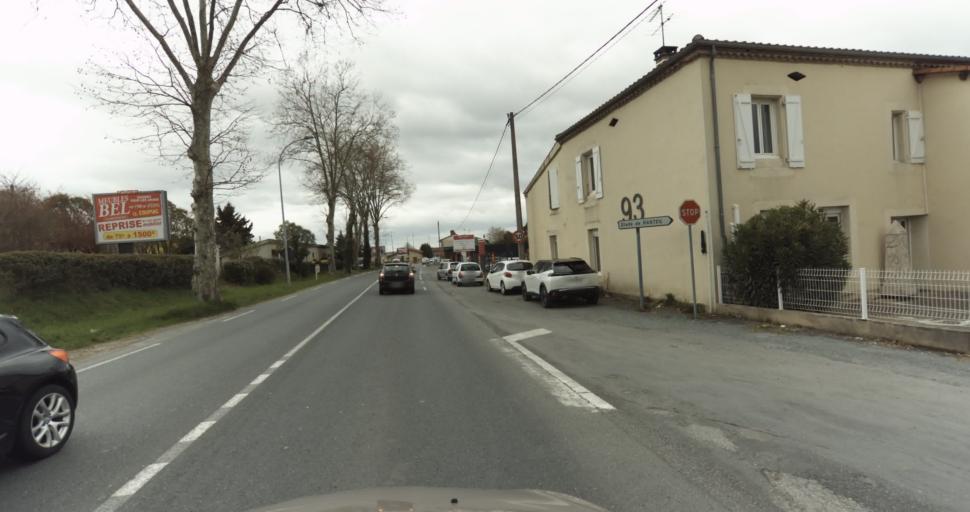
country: FR
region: Midi-Pyrenees
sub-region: Departement du Tarn
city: Puygouzon
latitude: 43.9042
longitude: 2.1427
